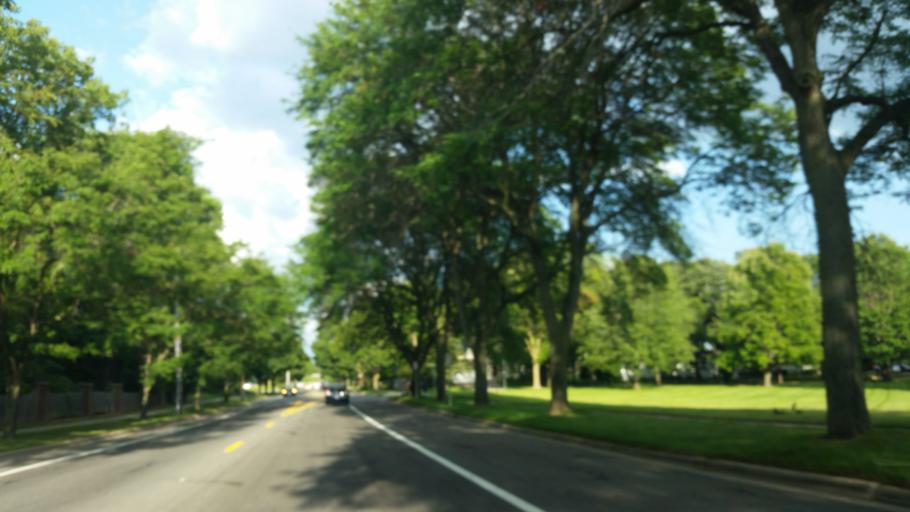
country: US
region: Wisconsin
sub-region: Dane County
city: Shorewood Hills
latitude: 43.0464
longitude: -89.4803
